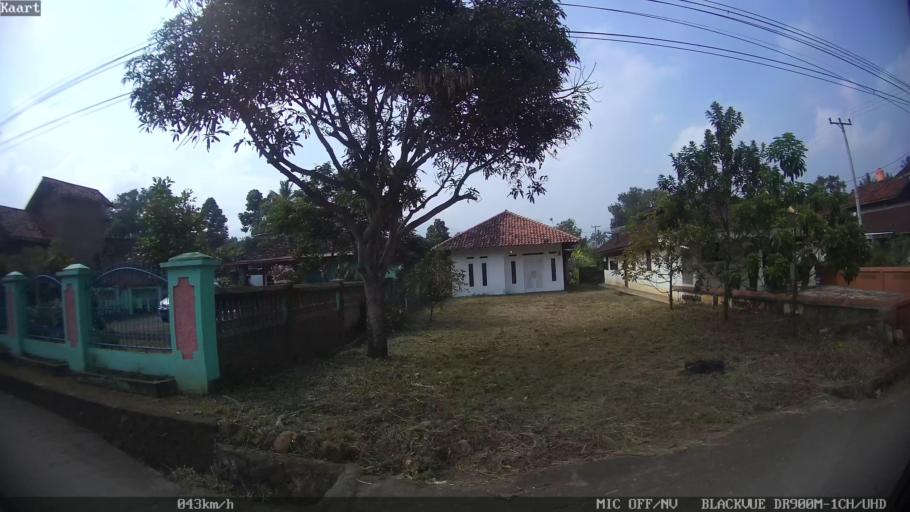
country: ID
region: Lampung
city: Gedongtataan
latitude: -5.3791
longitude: 105.1239
